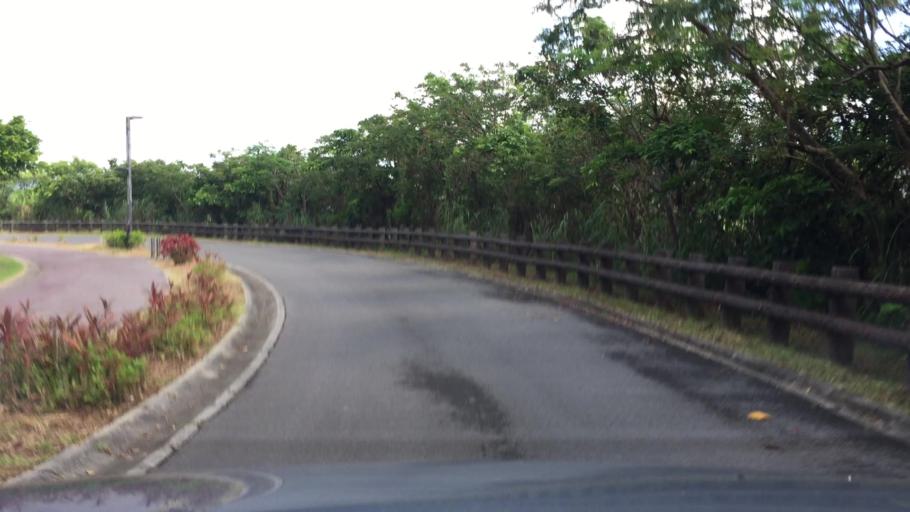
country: JP
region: Okinawa
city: Ishigaki
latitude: 24.3866
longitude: 124.1690
